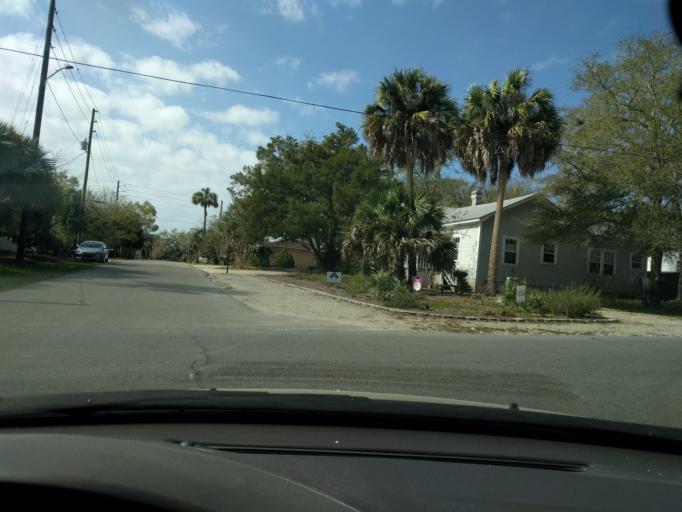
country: US
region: Florida
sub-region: Franklin County
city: Apalachicola
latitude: 29.7294
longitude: -84.9897
